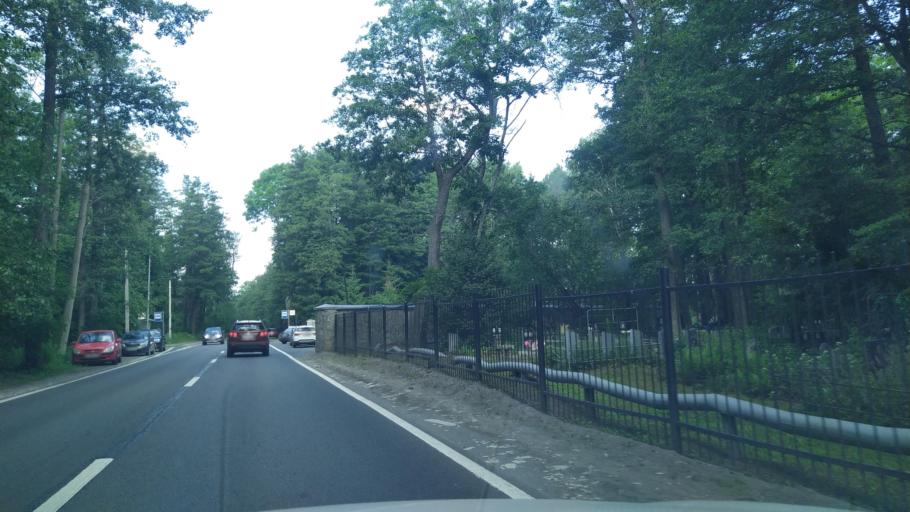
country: RU
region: St.-Petersburg
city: Kronshtadt
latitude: 60.0173
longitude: 29.7068
